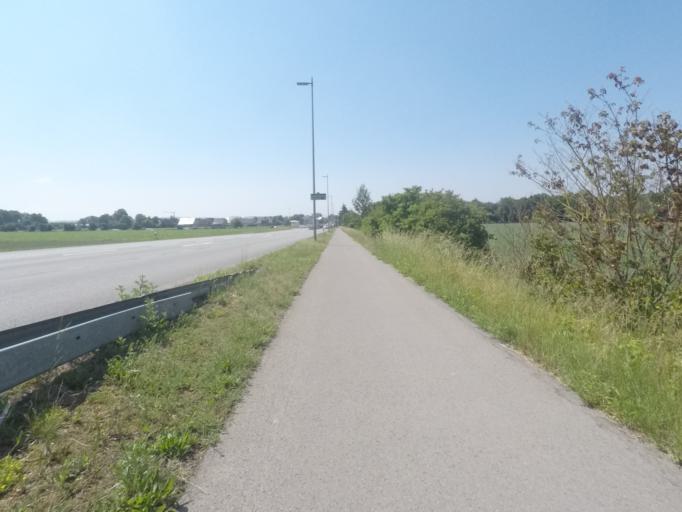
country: DE
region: North Rhine-Westphalia
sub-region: Regierungsbezirk Detmold
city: Bielefeld
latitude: 52.0386
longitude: 8.6160
